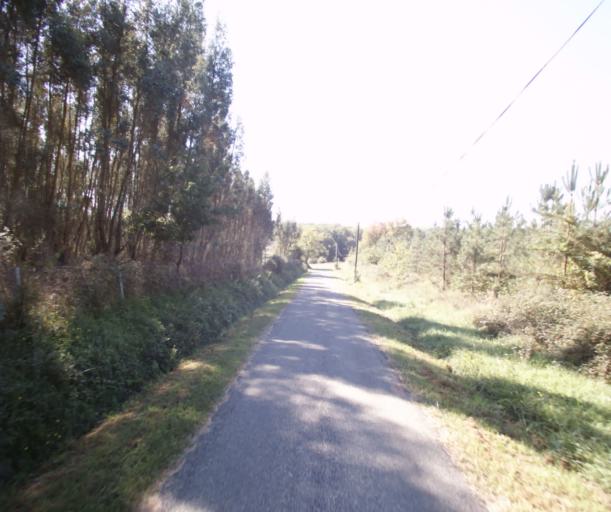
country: FR
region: Midi-Pyrenees
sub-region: Departement du Gers
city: Cazaubon
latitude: 43.9360
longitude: -0.0285
